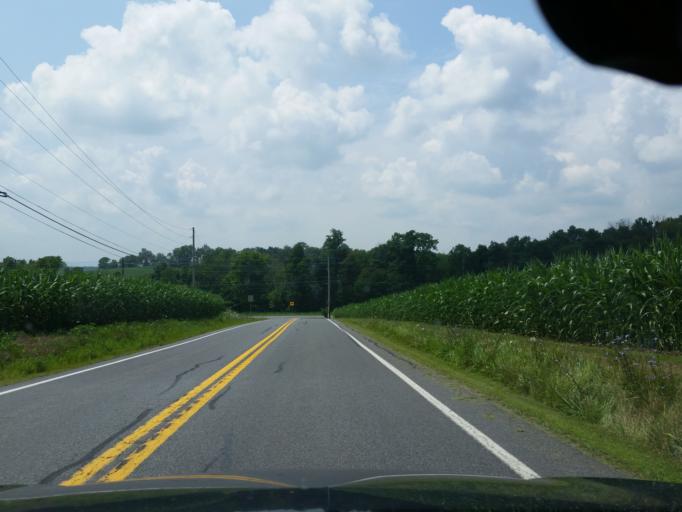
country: US
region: Pennsylvania
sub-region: Union County
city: Mifflinburg
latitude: 40.9937
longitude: -76.9900
